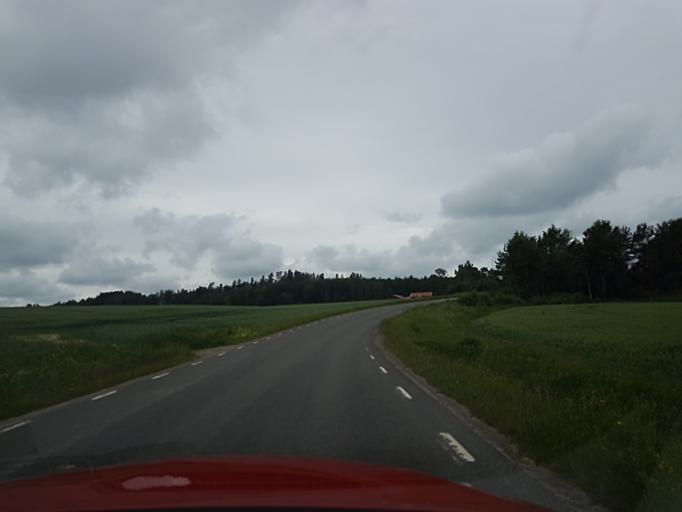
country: SE
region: Vaestra Goetaland
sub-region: Tibro Kommun
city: Tibro
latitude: 58.3055
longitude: 14.1188
